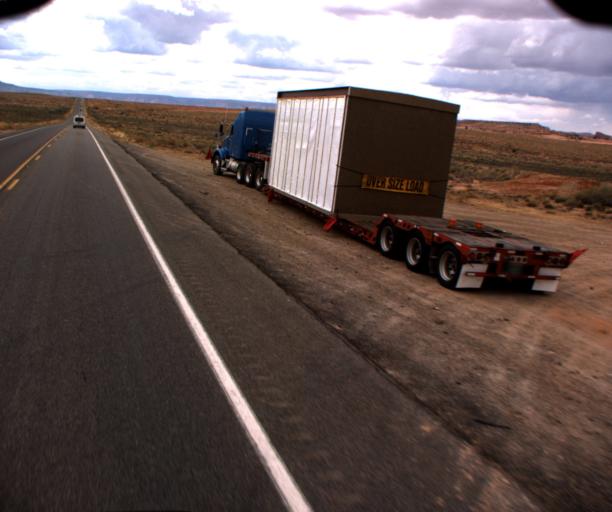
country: US
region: Arizona
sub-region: Navajo County
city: Kayenta
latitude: 36.7245
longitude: -110.1385
